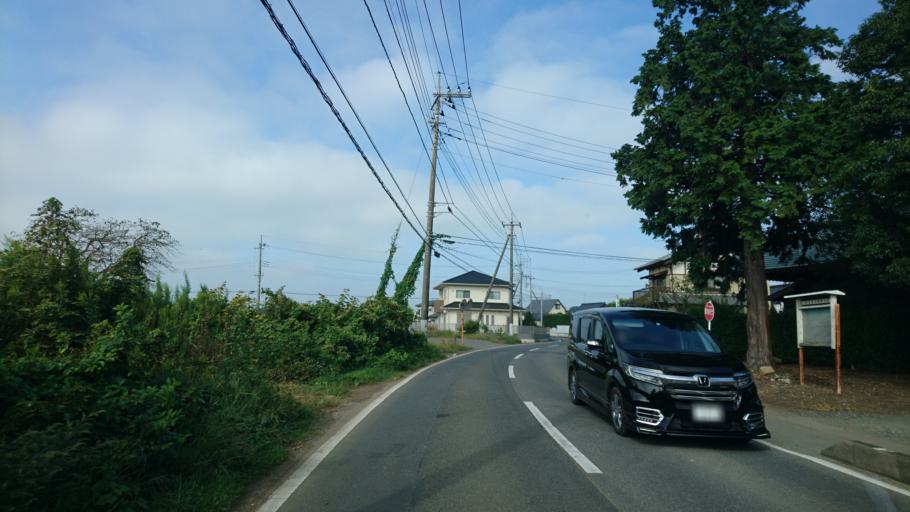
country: JP
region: Ibaraki
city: Naka
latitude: 36.0438
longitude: 140.0912
